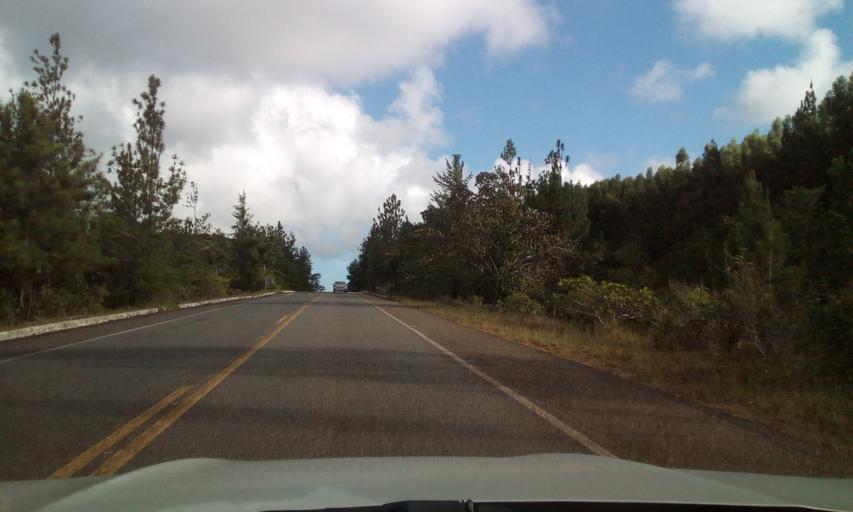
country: BR
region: Bahia
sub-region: Entre Rios
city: Entre Rios
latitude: -12.1357
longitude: -37.7916
